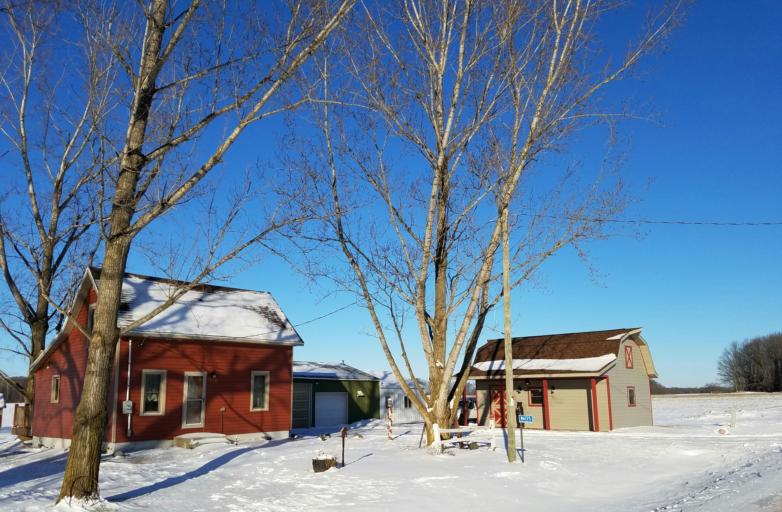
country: US
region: Wisconsin
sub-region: Marathon County
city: Spencer
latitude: 44.6634
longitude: -90.3168
